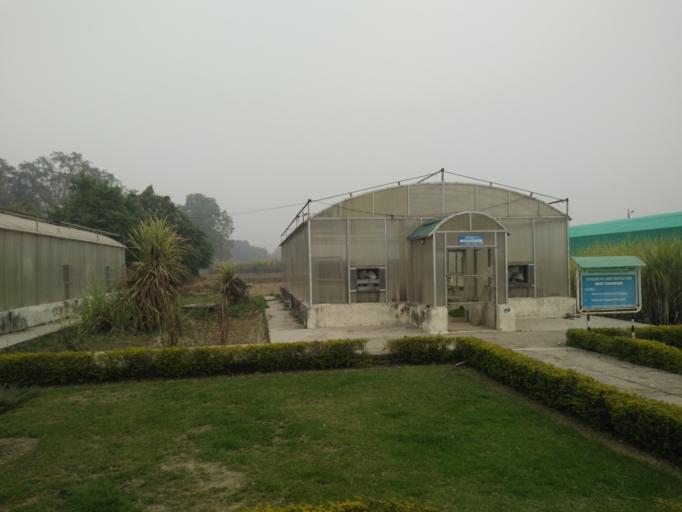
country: IN
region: Uttar Pradesh
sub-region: Lucknow District
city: Lucknow
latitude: 26.8024
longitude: 80.9332
